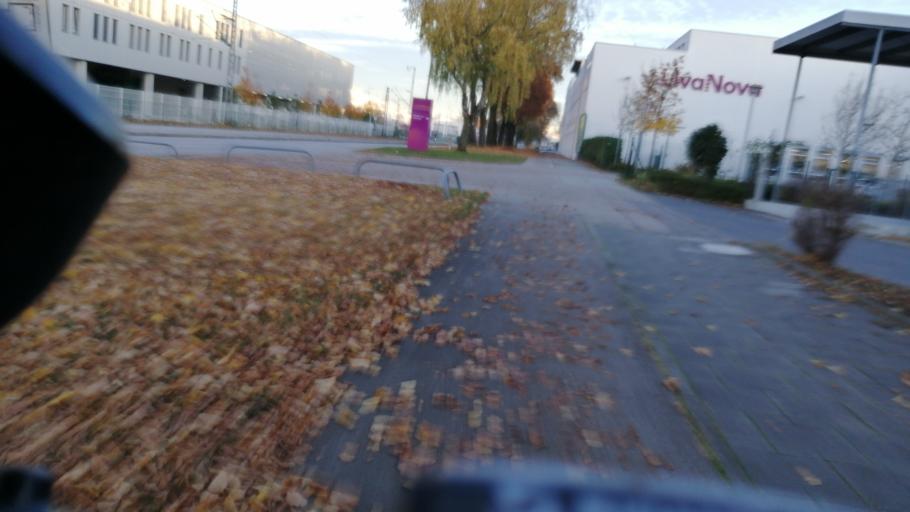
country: DE
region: Bavaria
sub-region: Upper Bavaria
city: Unterfoehring
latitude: 48.1923
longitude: 11.6037
